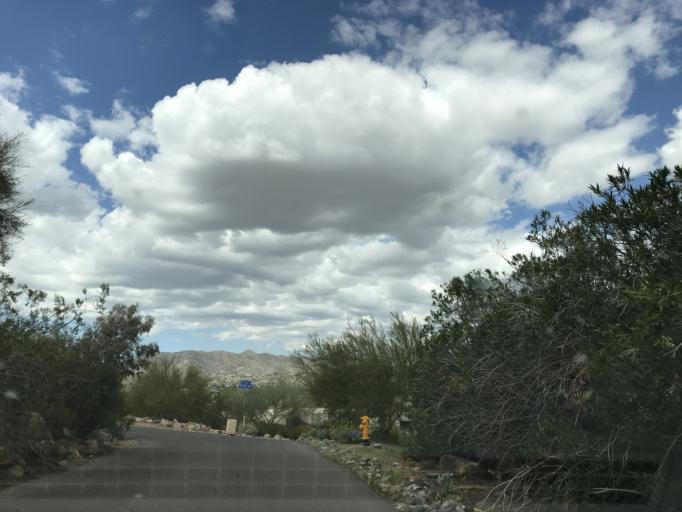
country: US
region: Arizona
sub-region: Maricopa County
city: Paradise Valley
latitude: 33.5213
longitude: -111.9574
